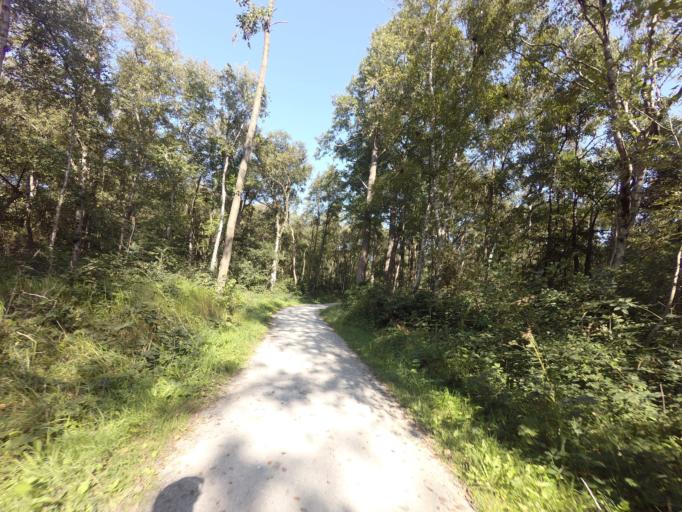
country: NL
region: Friesland
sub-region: Gemeente Schiermonnikoog
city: Schiermonnikoog
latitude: 53.4868
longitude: 6.1729
